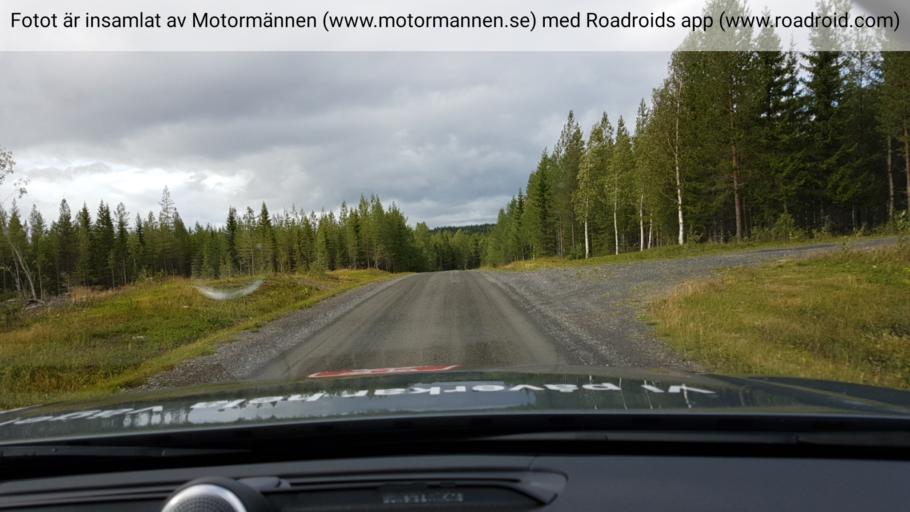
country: SE
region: Jaemtland
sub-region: OEstersunds Kommun
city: Lit
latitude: 63.7659
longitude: 14.6601
